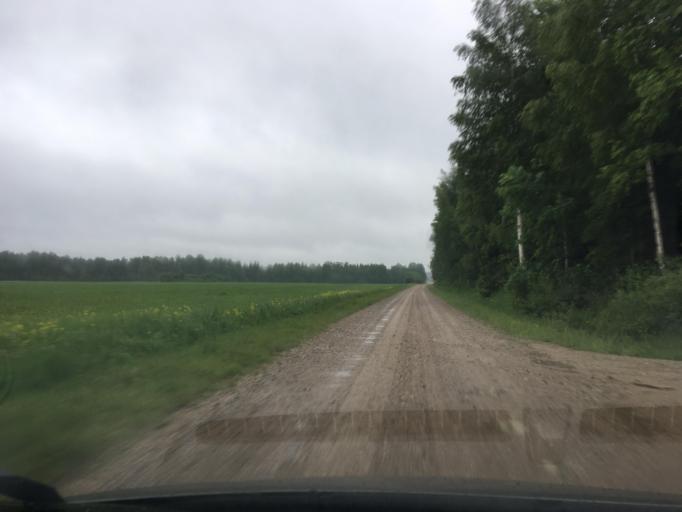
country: EE
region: Laeaene
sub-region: Lihula vald
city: Lihula
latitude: 58.6254
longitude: 23.8183
